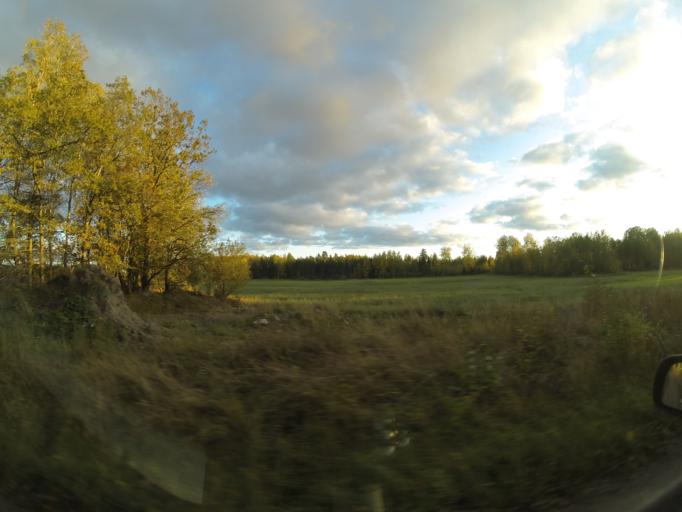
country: SE
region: Soedermanland
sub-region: Eskilstuna Kommun
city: Kvicksund
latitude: 59.4817
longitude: 16.3181
